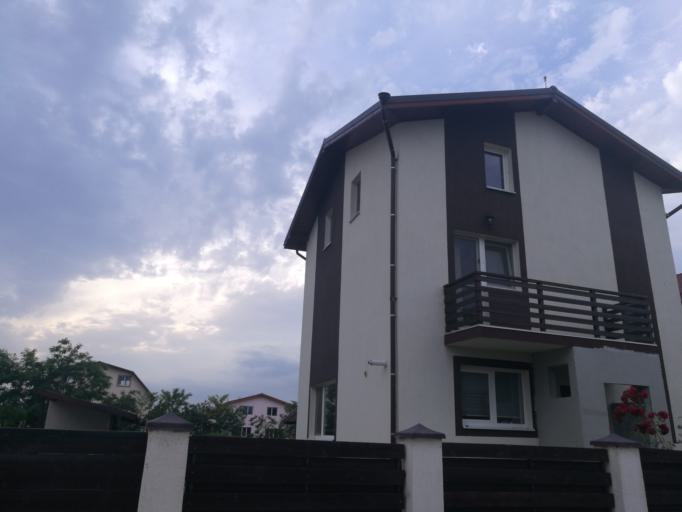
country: RO
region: Ilfov
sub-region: Comuna Vidra
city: Vidra
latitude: 44.2774
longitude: 26.1848
